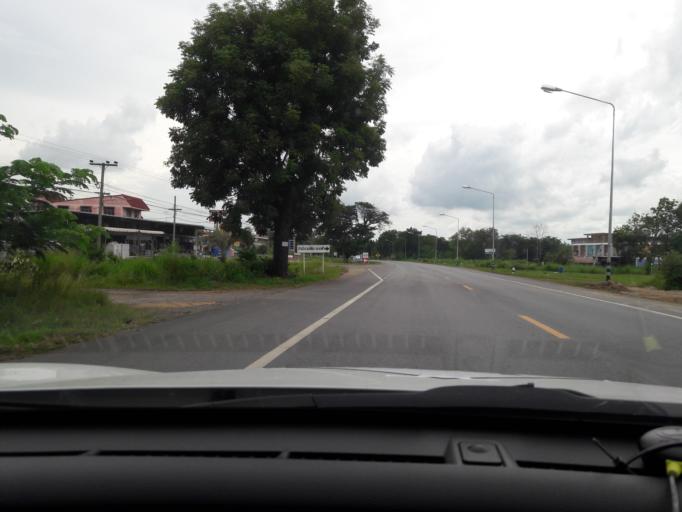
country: TH
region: Nakhon Sawan
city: Tak Fa
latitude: 15.3602
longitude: 100.5034
